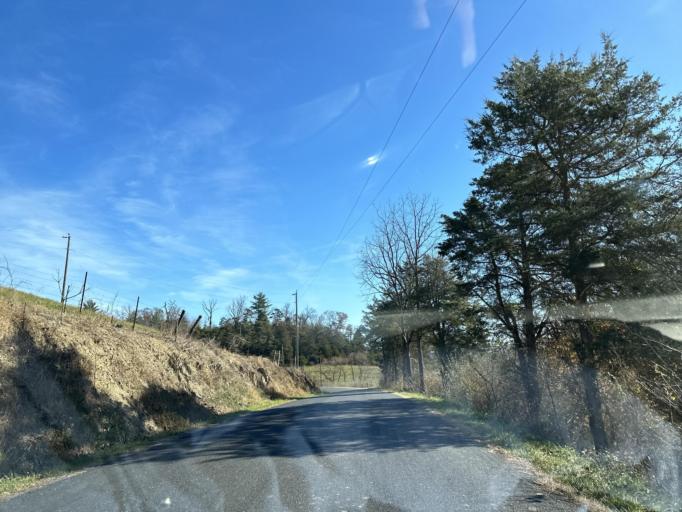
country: US
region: Virginia
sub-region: Augusta County
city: Weyers Cave
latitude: 38.2365
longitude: -78.9242
